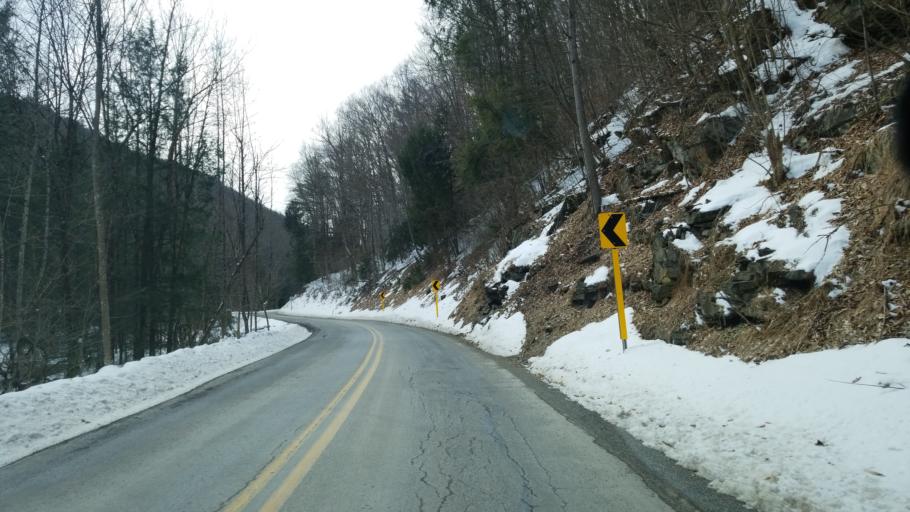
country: US
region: Pennsylvania
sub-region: Cameron County
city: Emporium
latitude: 41.2746
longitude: -78.1435
